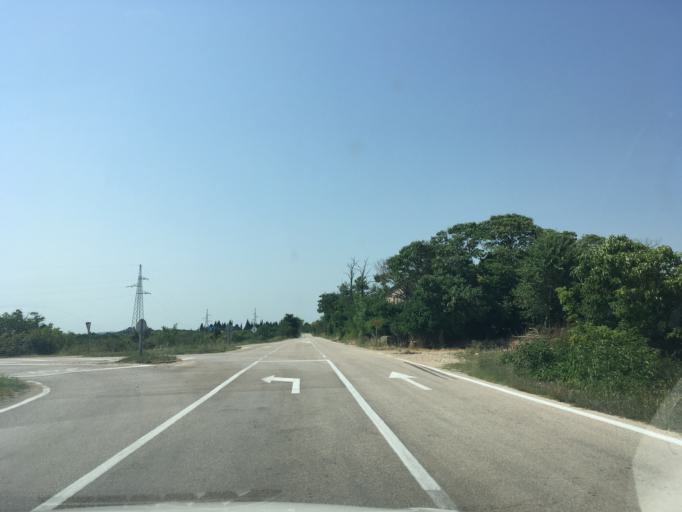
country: HR
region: Zadarska
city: Benkovac
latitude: 44.0242
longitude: 15.6333
